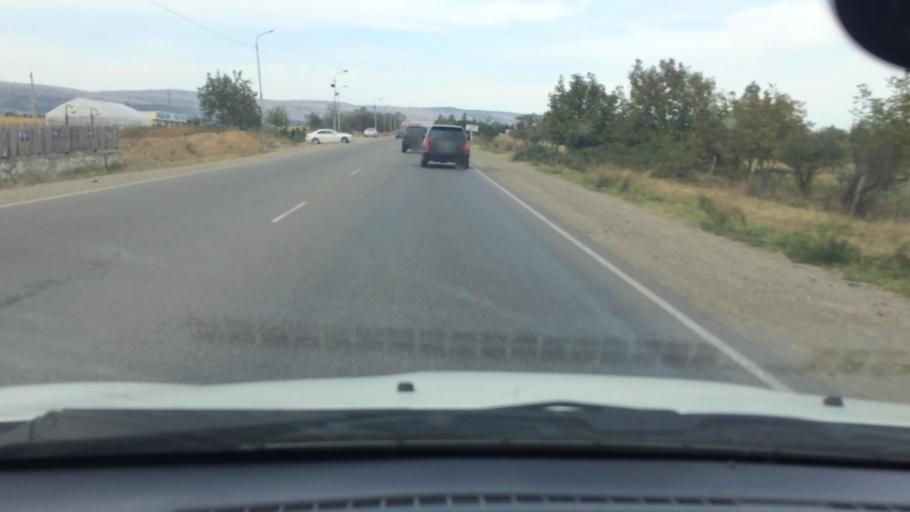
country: GE
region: Kvemo Kartli
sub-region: Marneuli
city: Marneuli
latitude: 41.5865
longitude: 44.7791
